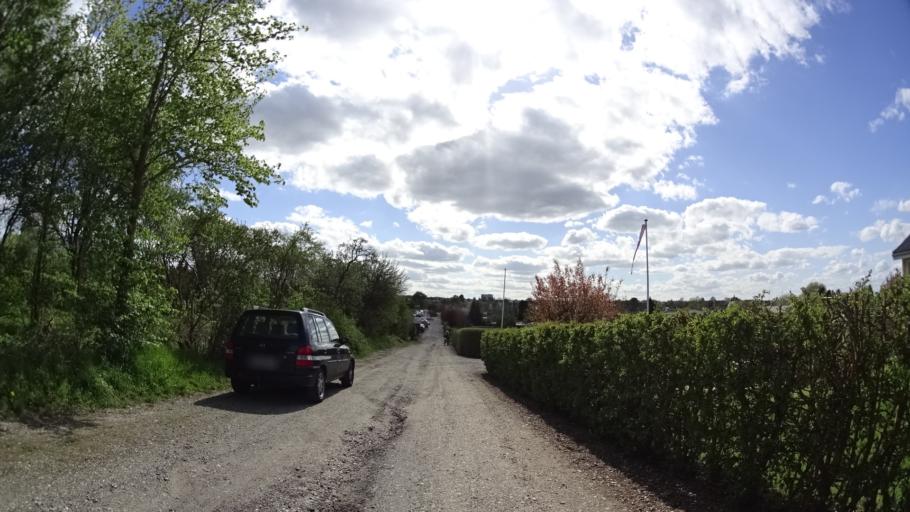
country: DK
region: Central Jutland
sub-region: Arhus Kommune
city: Stavtrup
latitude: 56.1352
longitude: 10.1658
